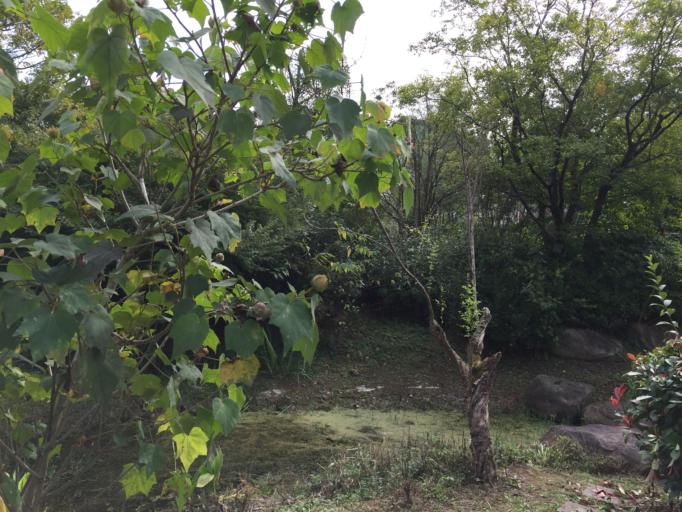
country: CN
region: Anhui Sheng
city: Xintan
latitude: 29.7247
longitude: 118.2821
